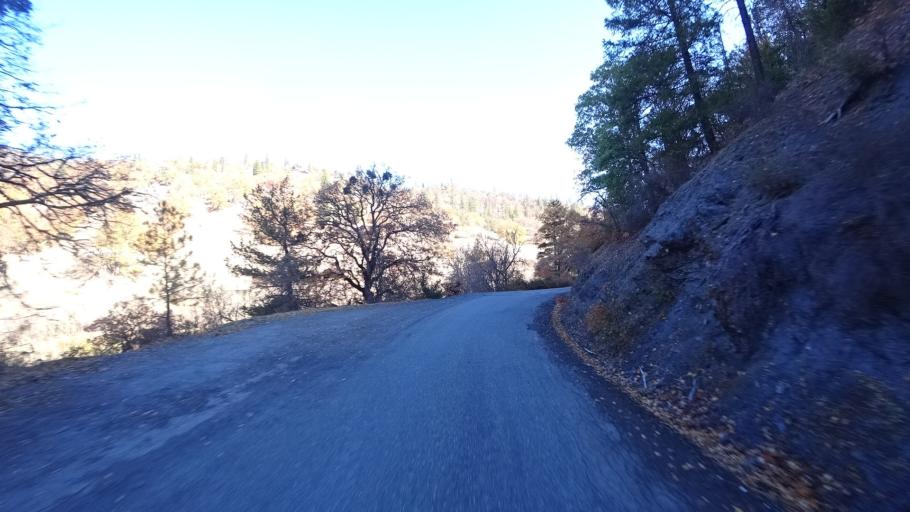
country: US
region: California
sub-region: Siskiyou County
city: Yreka
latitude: 41.8401
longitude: -122.9250
